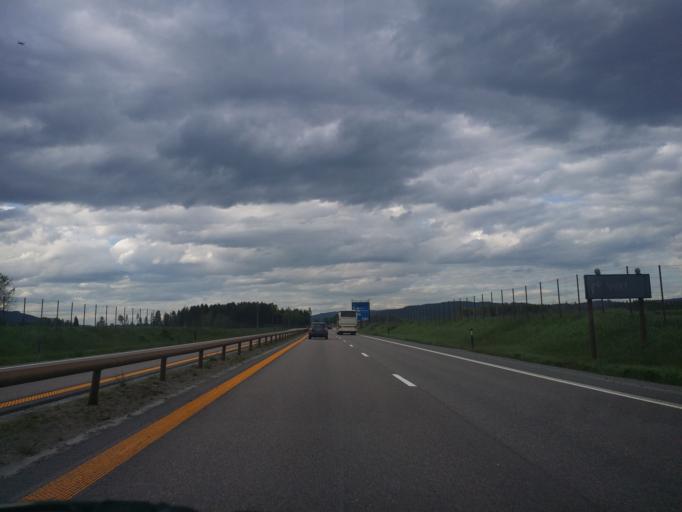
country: NO
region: Akershus
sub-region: Eidsvoll
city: Eidsvoll
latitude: 60.3814
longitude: 11.2104
